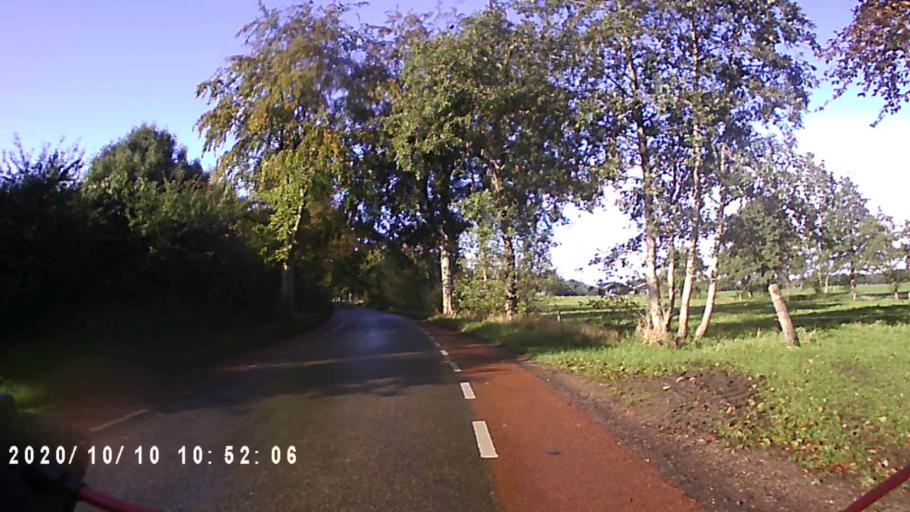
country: NL
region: Friesland
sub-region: Gemeente Achtkarspelen
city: Surhuisterveen
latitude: 53.1585
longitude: 6.2251
